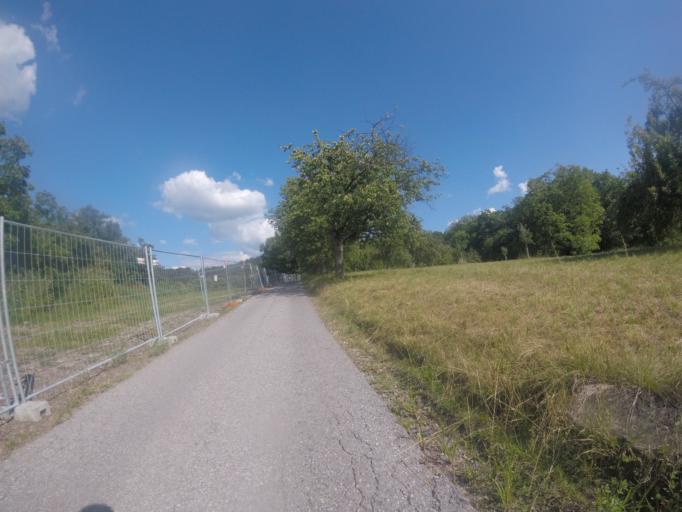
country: DE
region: Baden-Wuerttemberg
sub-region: Regierungsbezirk Stuttgart
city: Oberstenfeld
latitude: 49.0155
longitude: 9.3441
